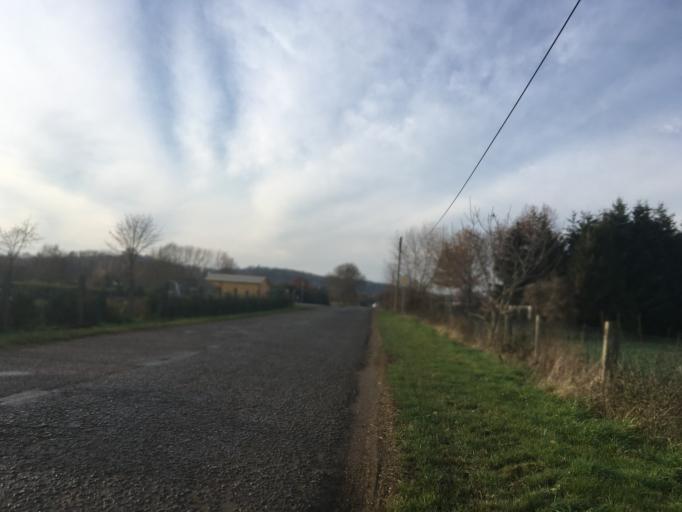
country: DE
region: Brandenburg
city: Bad Freienwalde
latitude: 52.7880
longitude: 14.0485
